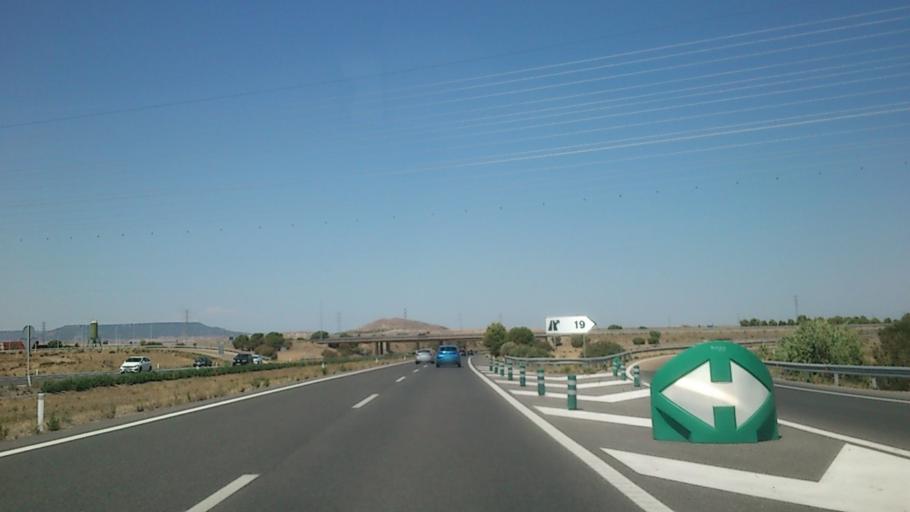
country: ES
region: Aragon
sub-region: Provincia de Zaragoza
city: Gallur
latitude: 41.8501
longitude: -1.3727
